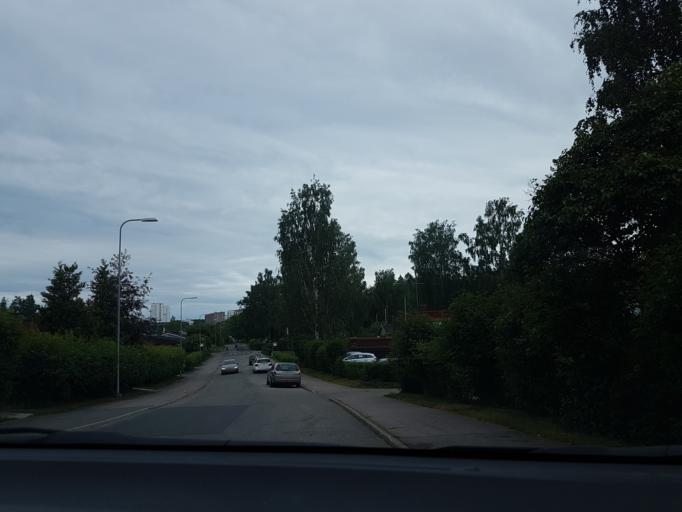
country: FI
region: Uusimaa
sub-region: Helsinki
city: Vantaa
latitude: 60.2117
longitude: 25.1255
